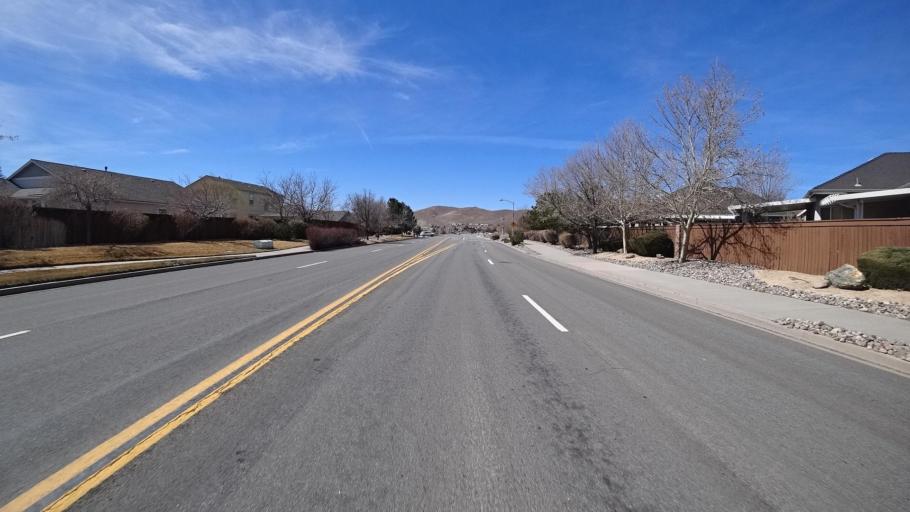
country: US
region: Nevada
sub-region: Washoe County
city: Sun Valley
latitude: 39.5860
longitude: -119.7278
